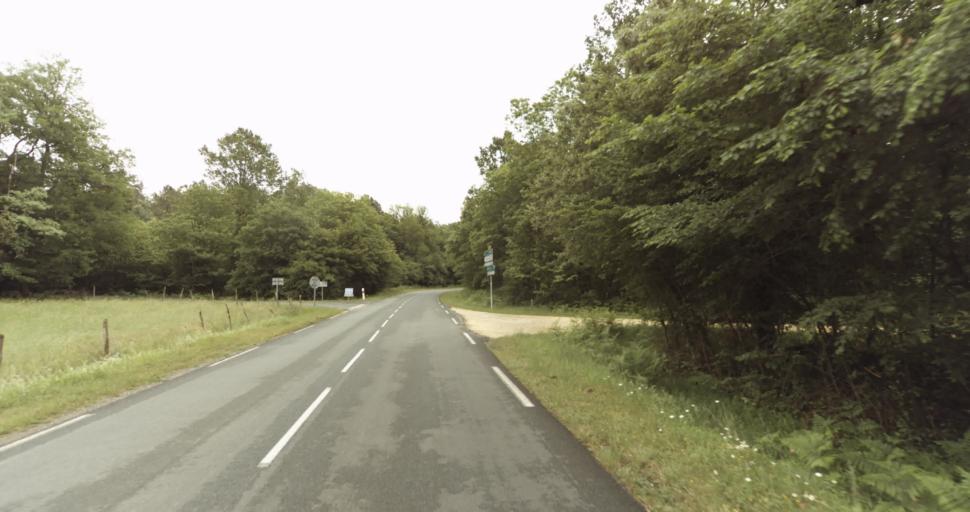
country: FR
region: Aquitaine
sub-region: Departement de la Dordogne
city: Belves
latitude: 44.6777
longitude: 0.9931
